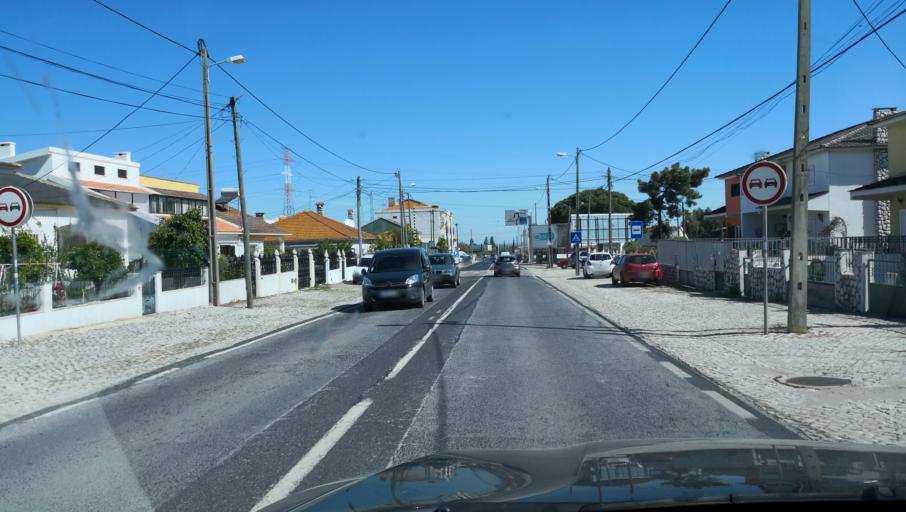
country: PT
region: Setubal
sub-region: Palmela
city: Palmela
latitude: 38.5817
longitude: -8.8902
